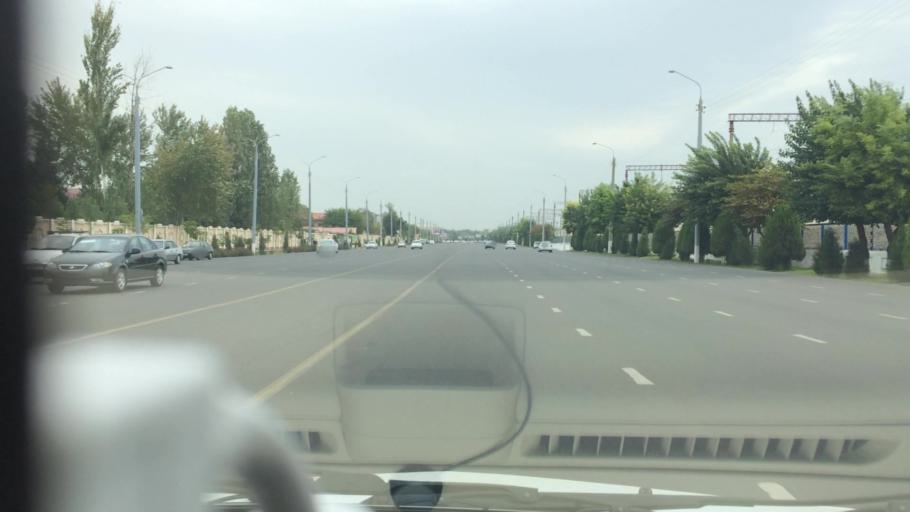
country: UZ
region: Toshkent Shahri
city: Tashkent
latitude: 41.2811
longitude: 69.2753
